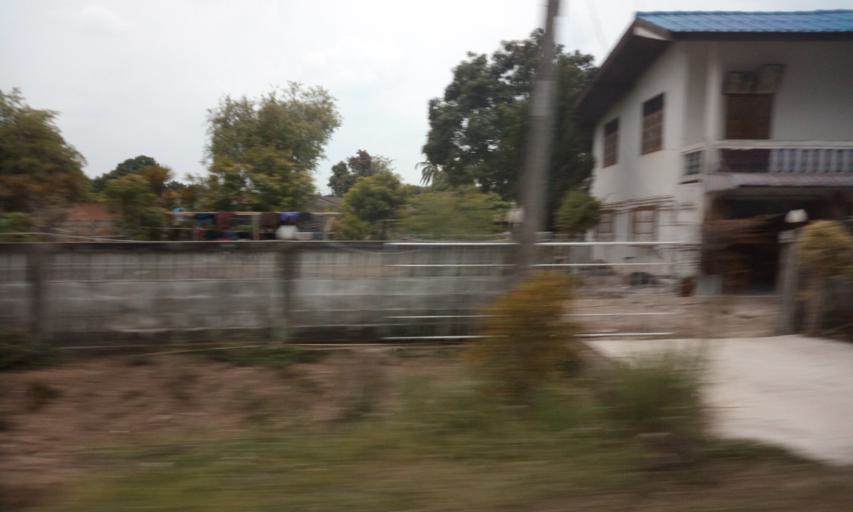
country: TH
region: Phayao
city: Chiang Kham
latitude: 19.5131
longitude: 100.3168
